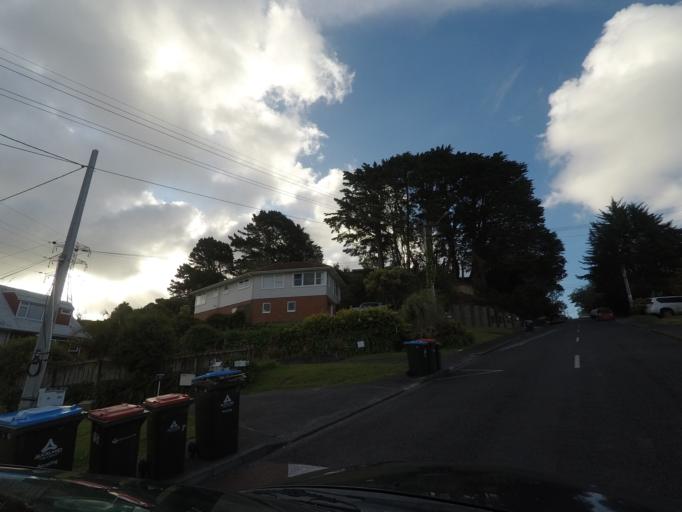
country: NZ
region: Auckland
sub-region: Auckland
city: Mangere
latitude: -36.9251
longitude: 174.7586
